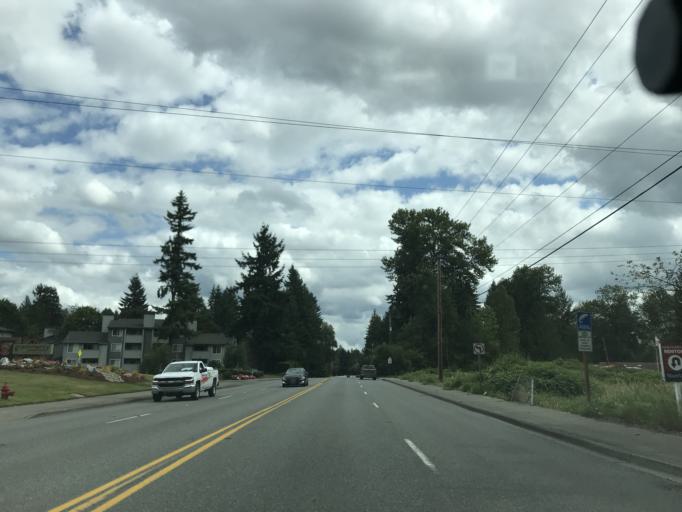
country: US
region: Washington
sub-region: King County
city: Fairwood
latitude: 47.4453
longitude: -122.1815
